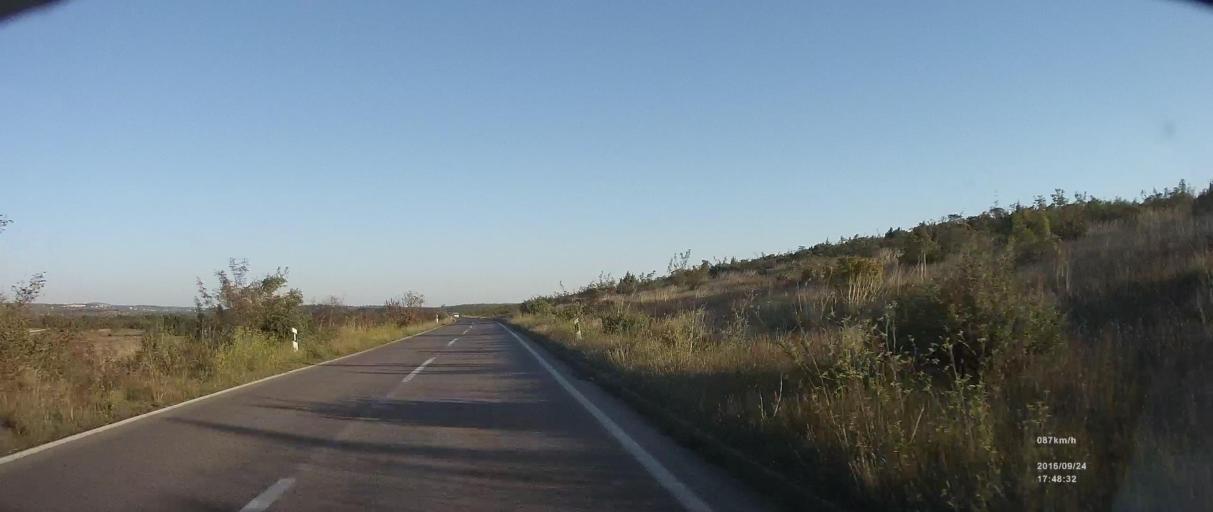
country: HR
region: Zadarska
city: Polaca
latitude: 44.0638
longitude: 15.5376
